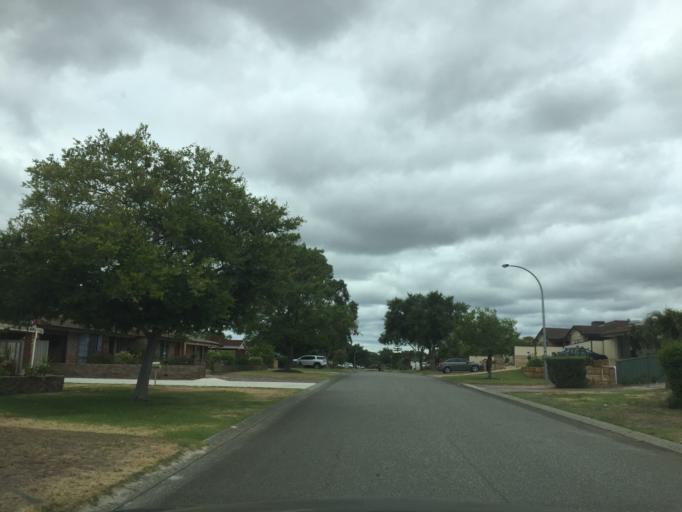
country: AU
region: Western Australia
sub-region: Gosnells
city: Thornlie
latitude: -32.0726
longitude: 115.9555
